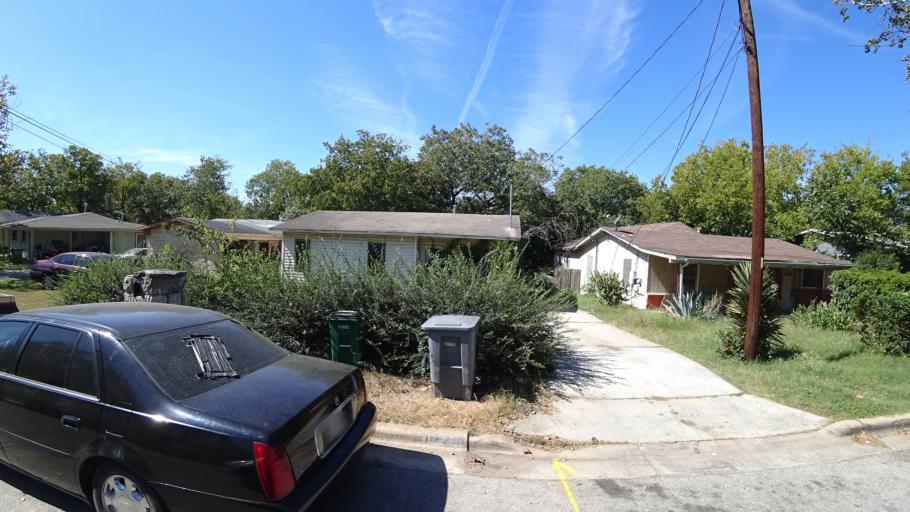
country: US
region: Texas
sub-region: Travis County
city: Austin
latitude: 30.2795
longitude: -97.6758
